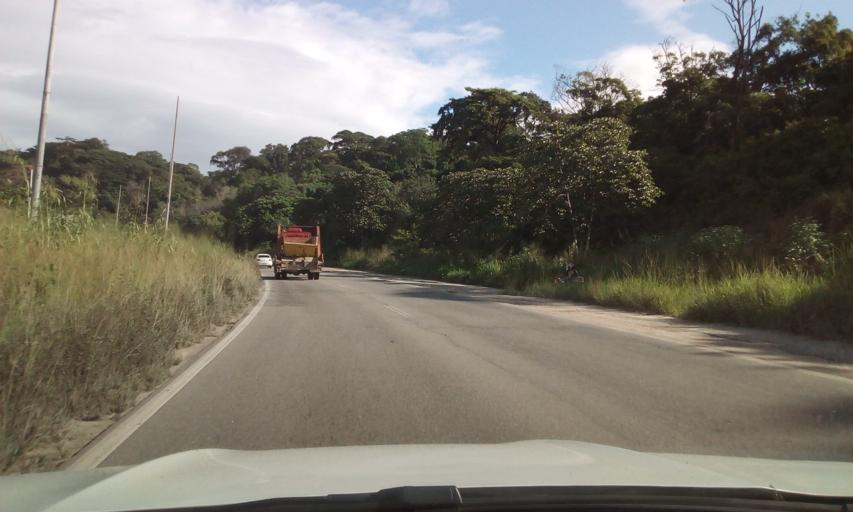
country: BR
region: Pernambuco
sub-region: Sao Lourenco Da Mata
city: Sao Lourenco da Mata
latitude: -7.9956
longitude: -34.9391
